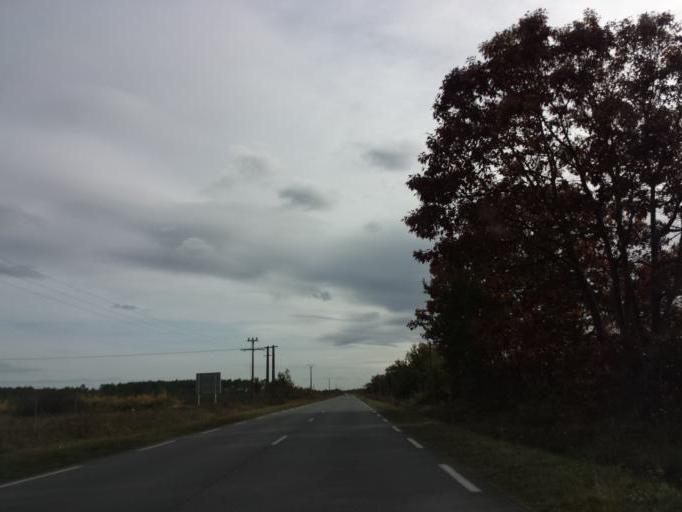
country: FR
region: Aquitaine
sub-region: Departement de la Gironde
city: Marcheprime
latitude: 44.7659
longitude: -0.9237
